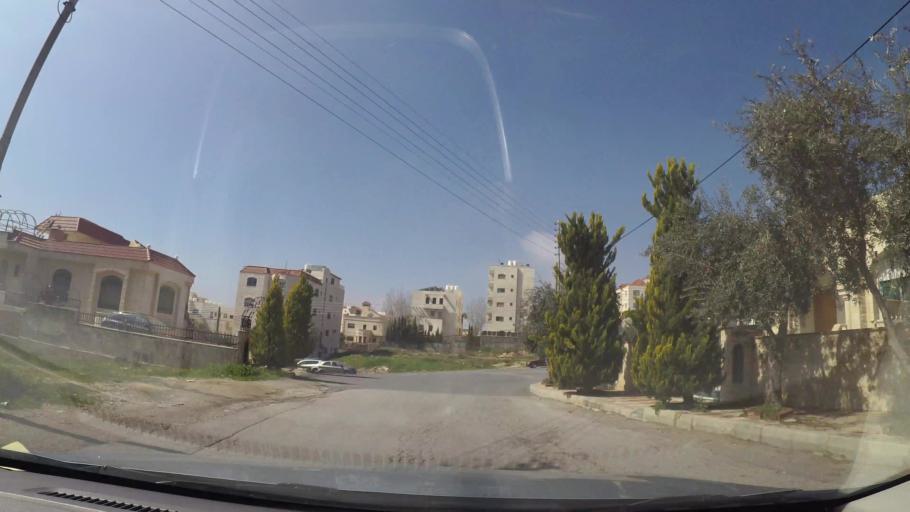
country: JO
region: Amman
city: Al Bunayyat ash Shamaliyah
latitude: 31.8975
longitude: 35.8770
